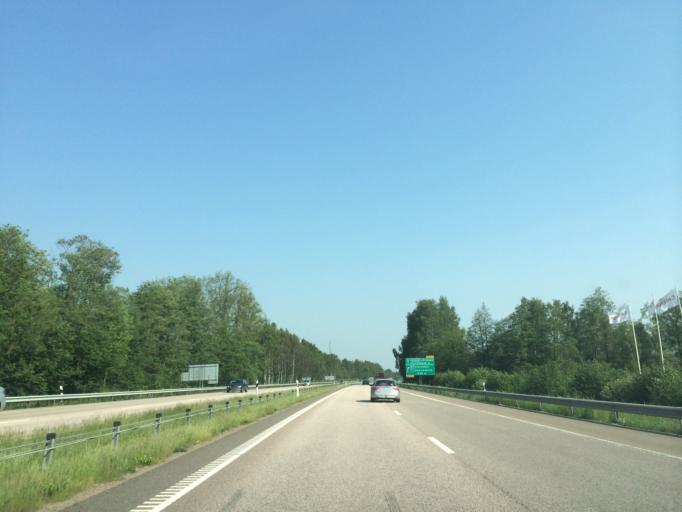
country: SE
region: Skane
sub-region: Helsingborg
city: Odakra
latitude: 56.0710
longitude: 12.7792
